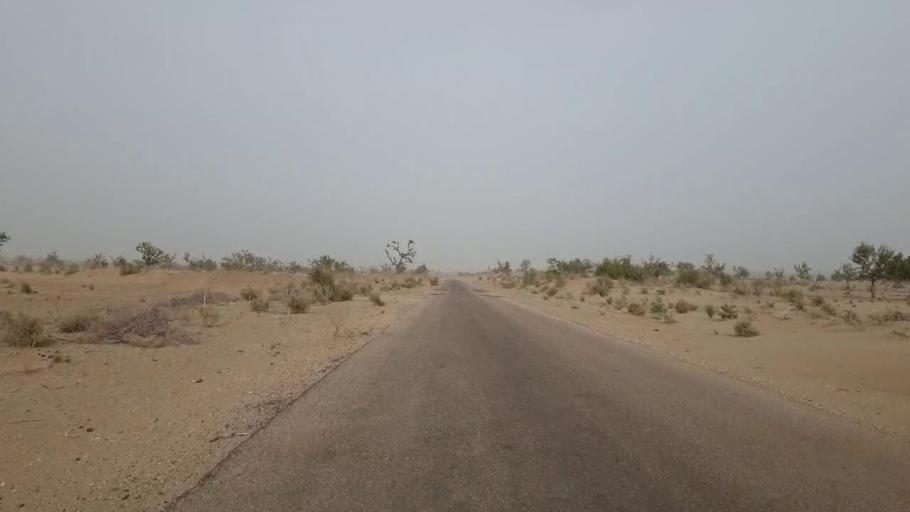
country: PK
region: Sindh
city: Islamkot
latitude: 24.5484
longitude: 70.3634
